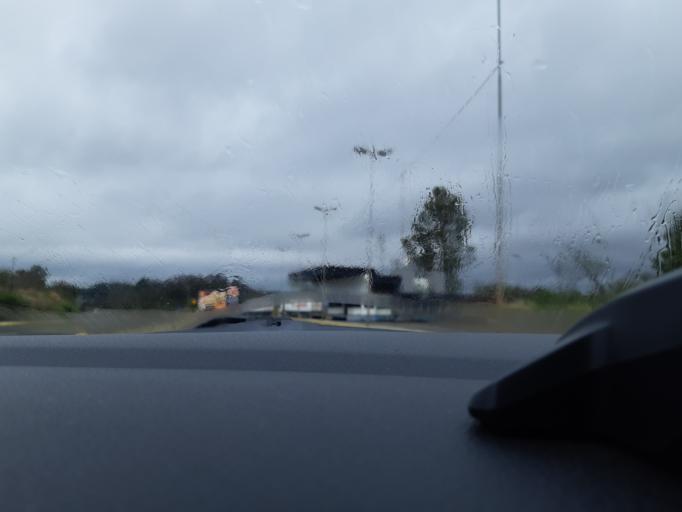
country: BR
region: Sao Paulo
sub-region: Ourinhos
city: Ourinhos
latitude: -23.0014
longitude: -49.9064
